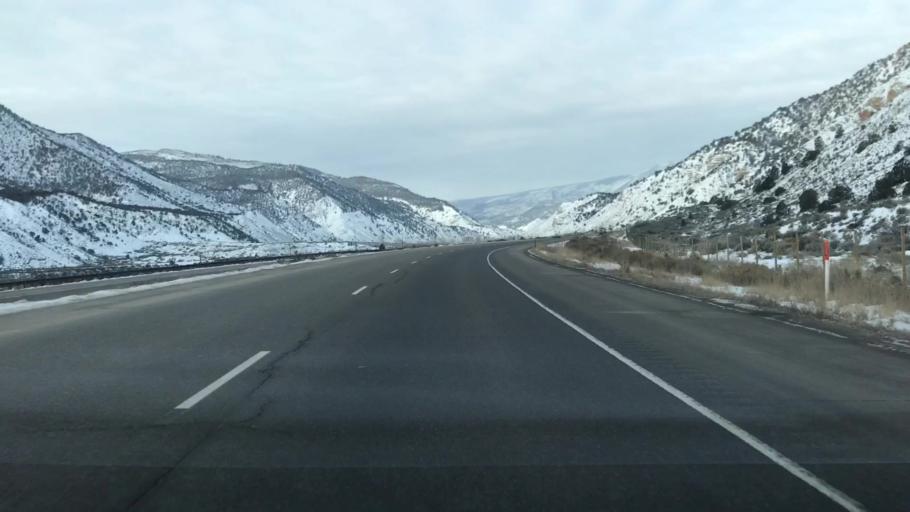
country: US
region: Colorado
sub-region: Eagle County
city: Gypsum
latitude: 39.6492
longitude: -106.9961
